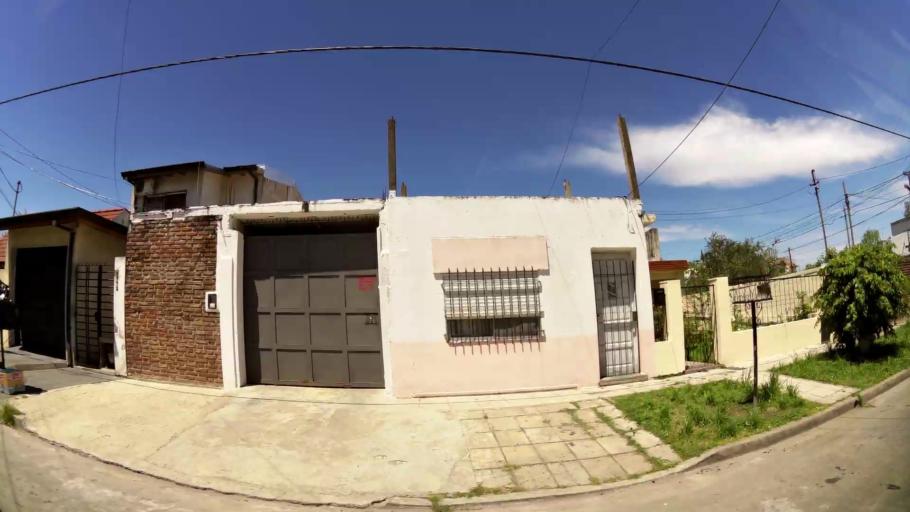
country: AR
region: Buenos Aires
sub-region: Partido de Quilmes
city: Quilmes
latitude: -34.7474
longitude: -58.2829
